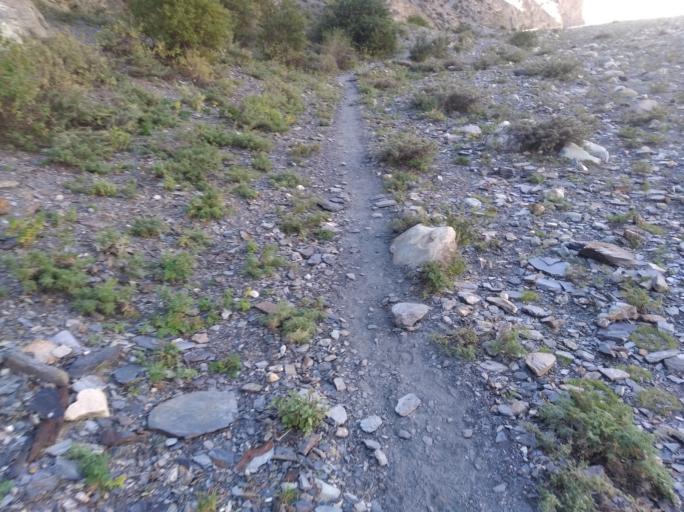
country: NP
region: Western Region
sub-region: Dhawalagiri Zone
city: Jomsom
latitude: 28.8645
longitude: 83.3443
